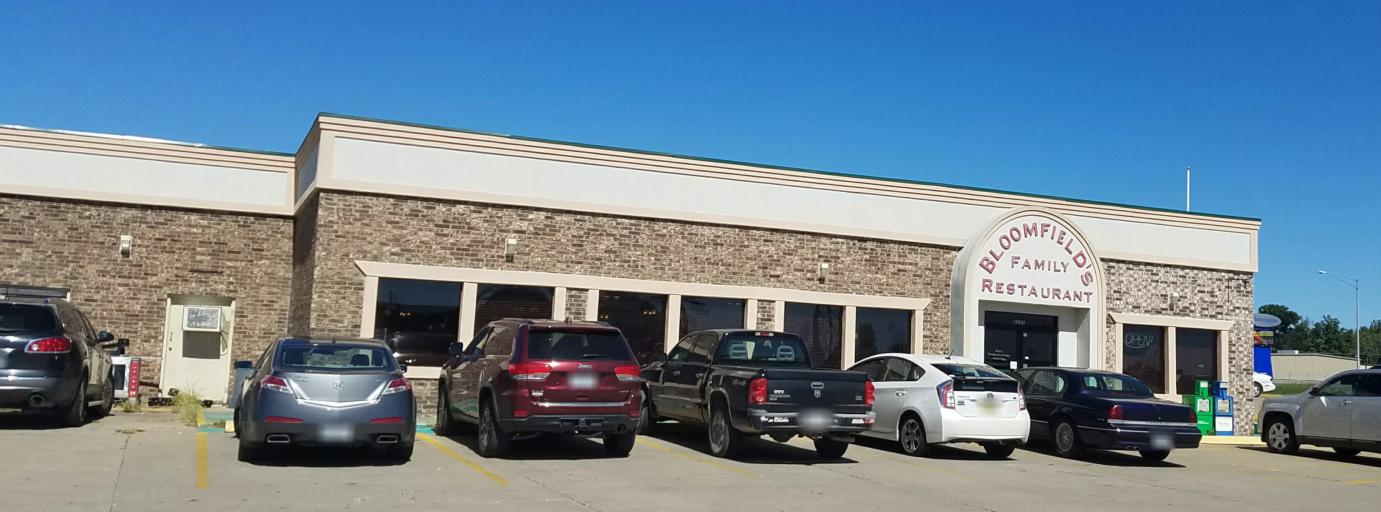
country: US
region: Missouri
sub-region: Saline County
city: Marshall
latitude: 39.1159
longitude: -93.2138
